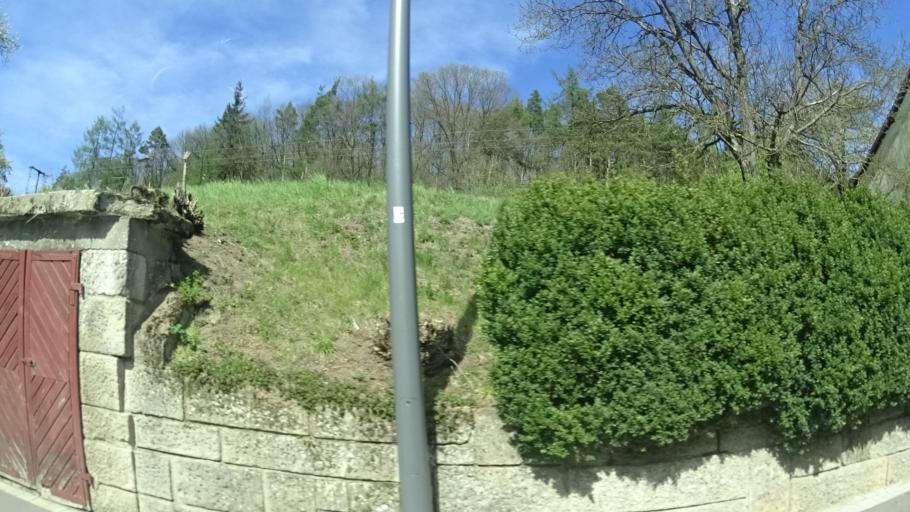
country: DE
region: Bavaria
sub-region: Regierungsbezirk Unterfranken
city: Burgpreppach
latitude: 50.1552
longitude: 10.6104
